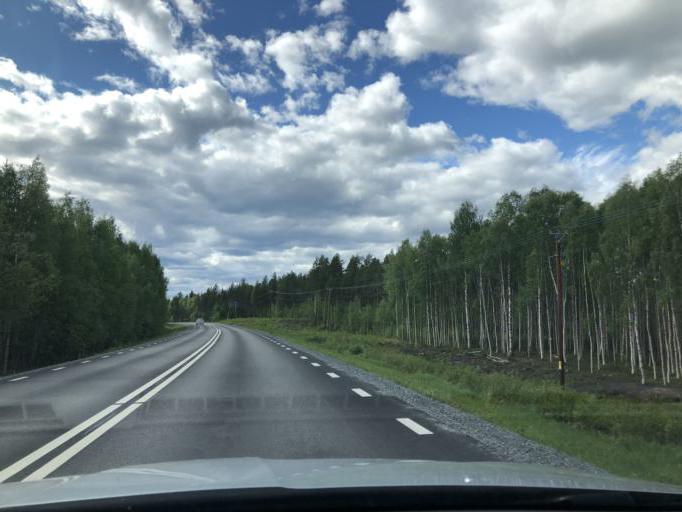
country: SE
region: Norrbotten
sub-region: Alvsbyns Kommun
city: AElvsbyn
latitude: 65.6926
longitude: 20.6798
